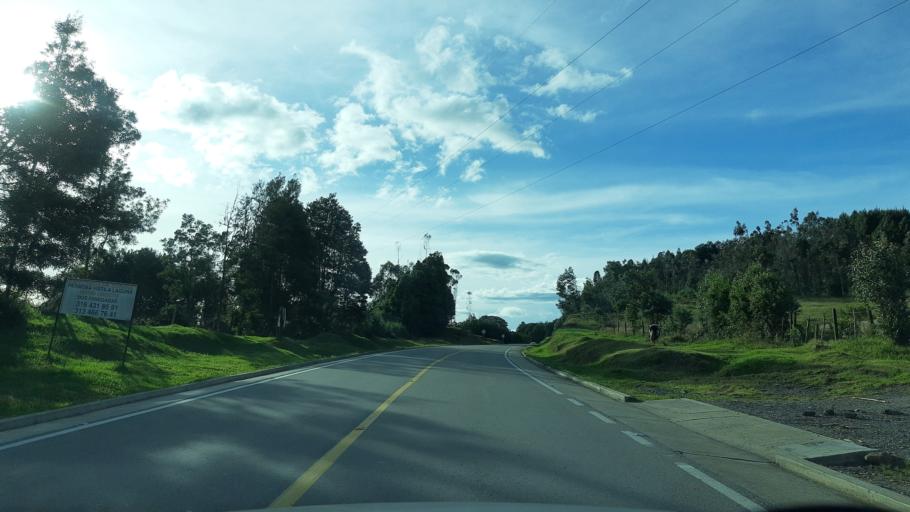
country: CO
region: Cundinamarca
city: Choconta
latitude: 5.0979
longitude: -73.6890
